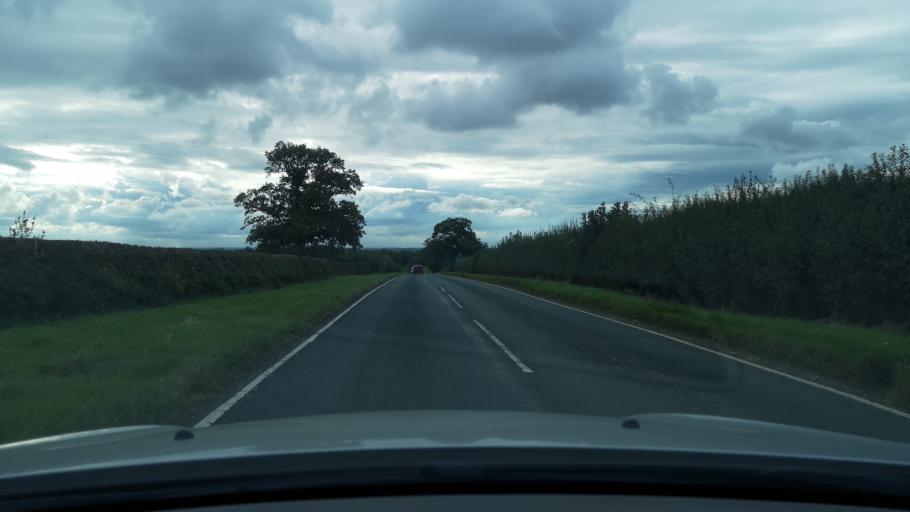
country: GB
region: England
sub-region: East Riding of Yorkshire
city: Hotham
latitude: 53.7887
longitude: -0.6255
